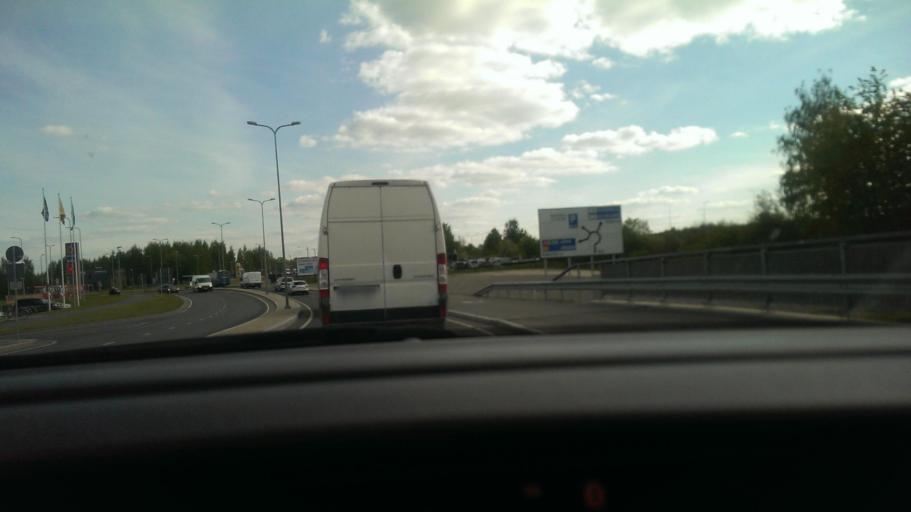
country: EE
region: Tartu
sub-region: UElenurme vald
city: Ulenurme
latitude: 58.3437
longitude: 26.7139
